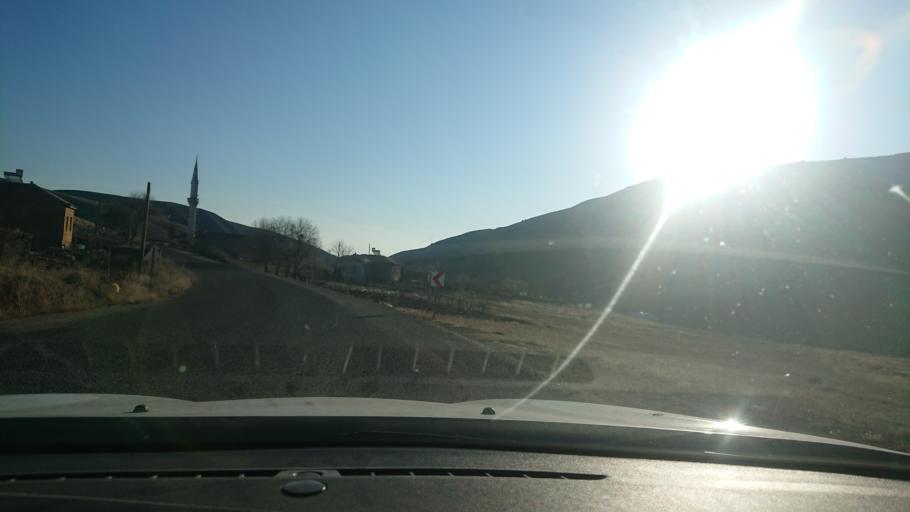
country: TR
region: Aksaray
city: Acipinar
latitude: 38.6938
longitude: 33.7479
